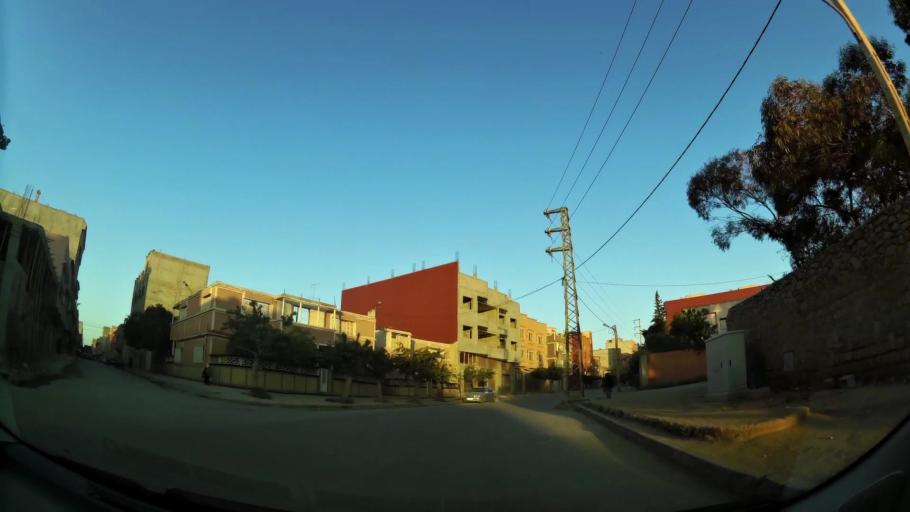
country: MA
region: Oriental
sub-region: Berkane-Taourirt
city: Berkane
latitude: 34.9181
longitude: -2.3254
